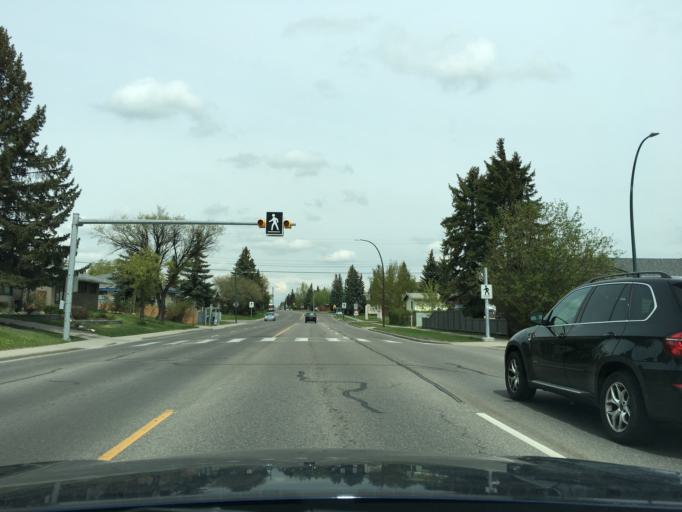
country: CA
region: Alberta
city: Calgary
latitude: 50.9560
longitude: -114.0848
